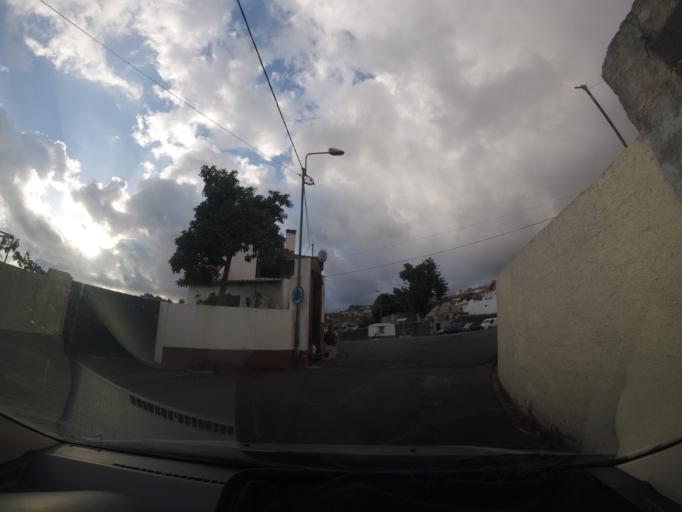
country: PT
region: Madeira
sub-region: Funchal
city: Nossa Senhora do Monte
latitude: 32.6647
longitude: -16.9317
